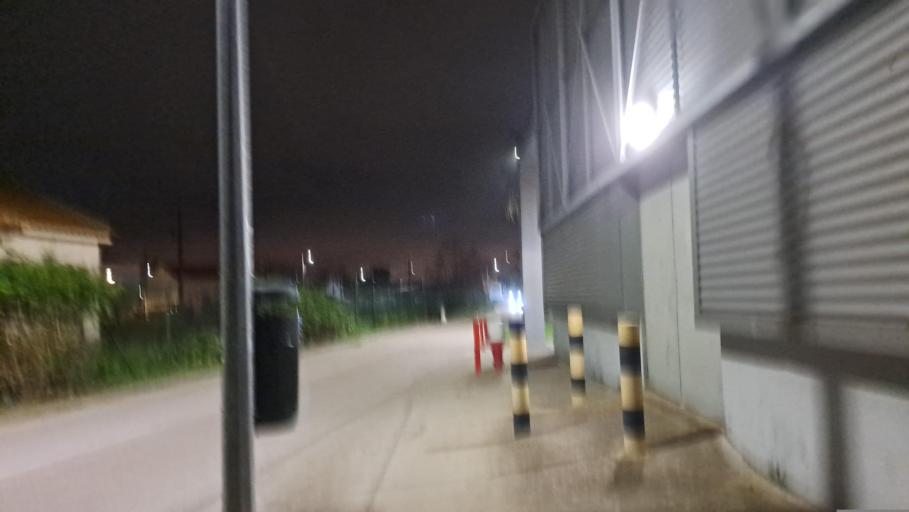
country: PT
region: Setubal
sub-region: Moita
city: Alhos Vedros
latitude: 38.6548
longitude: -9.0337
